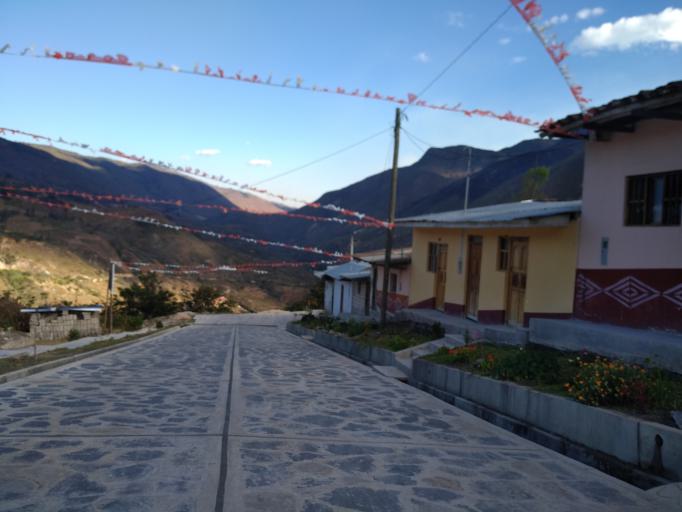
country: PE
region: Amazonas
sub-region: Provincia de Luya
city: Tingo
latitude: -6.3722
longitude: -77.9088
